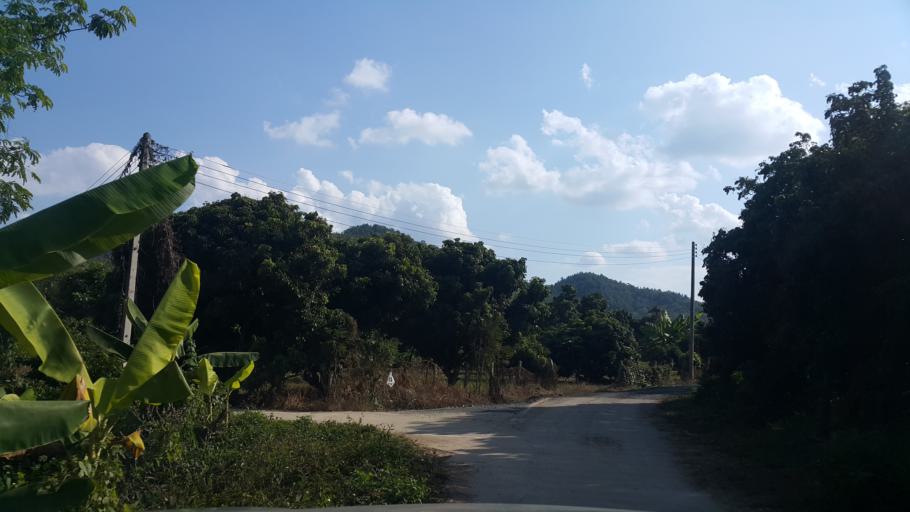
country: TH
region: Lamphun
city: Ban Thi
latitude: 18.5691
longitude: 99.1274
